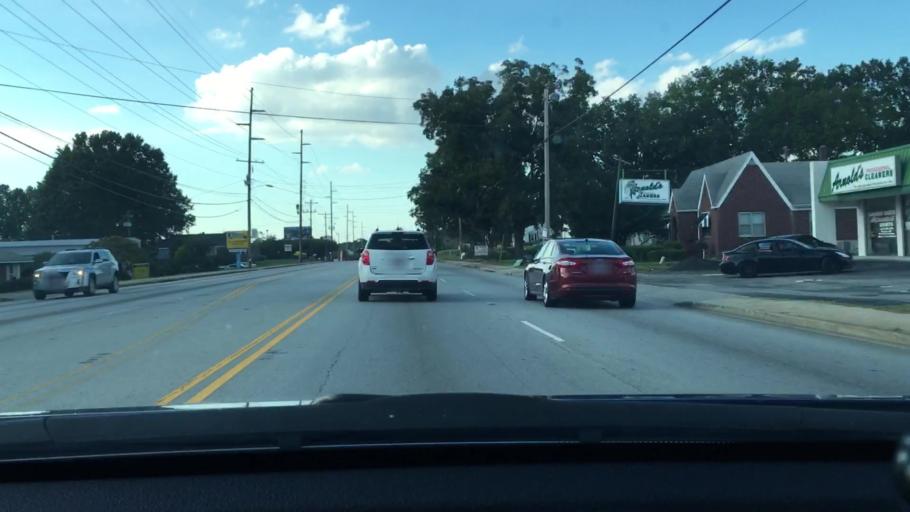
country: US
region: South Carolina
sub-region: Lexington County
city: Saint Andrews
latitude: 34.0505
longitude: -81.1061
